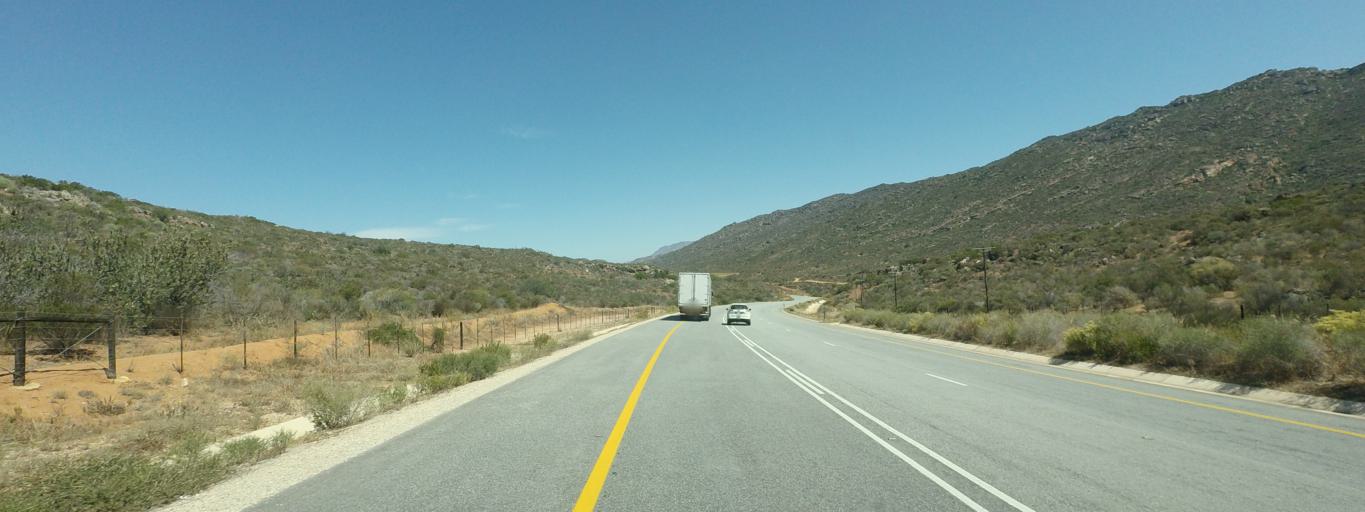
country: ZA
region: Western Cape
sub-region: West Coast District Municipality
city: Clanwilliam
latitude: -32.3338
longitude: 18.9249
